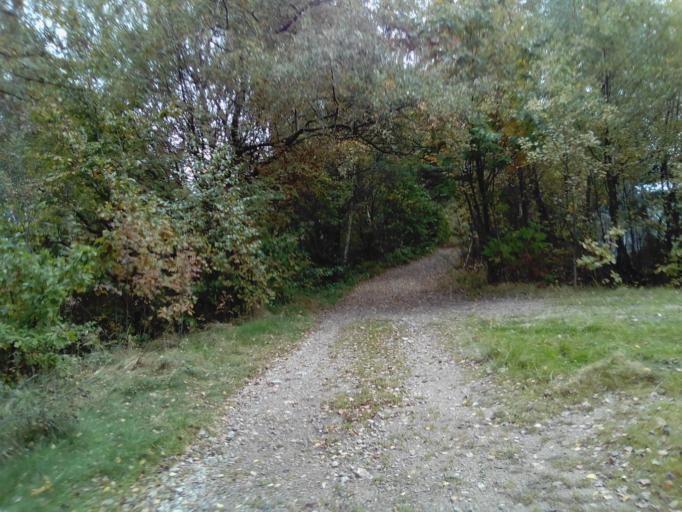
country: PL
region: Subcarpathian Voivodeship
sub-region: Powiat strzyzowski
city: Gwoznica Gorna
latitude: 49.8390
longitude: 22.0187
